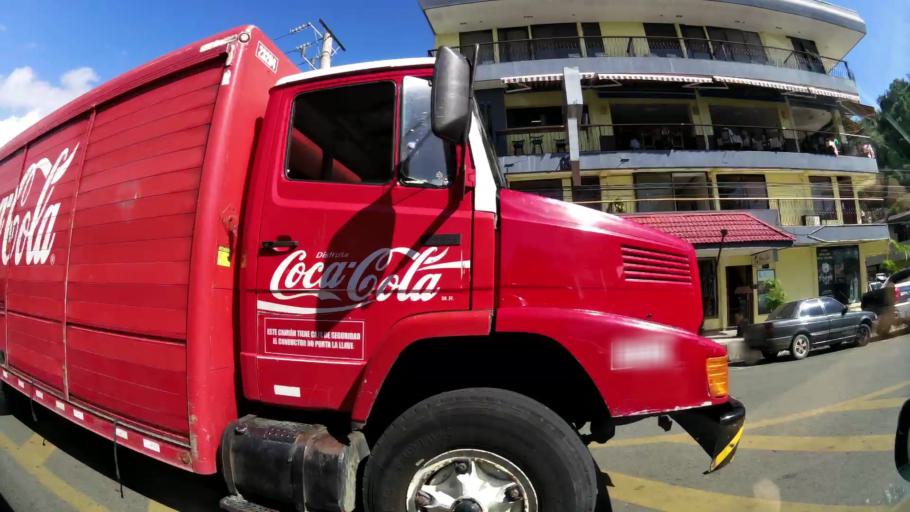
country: CR
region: Puntarenas
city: Quepos
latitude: 9.4308
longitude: -84.1651
